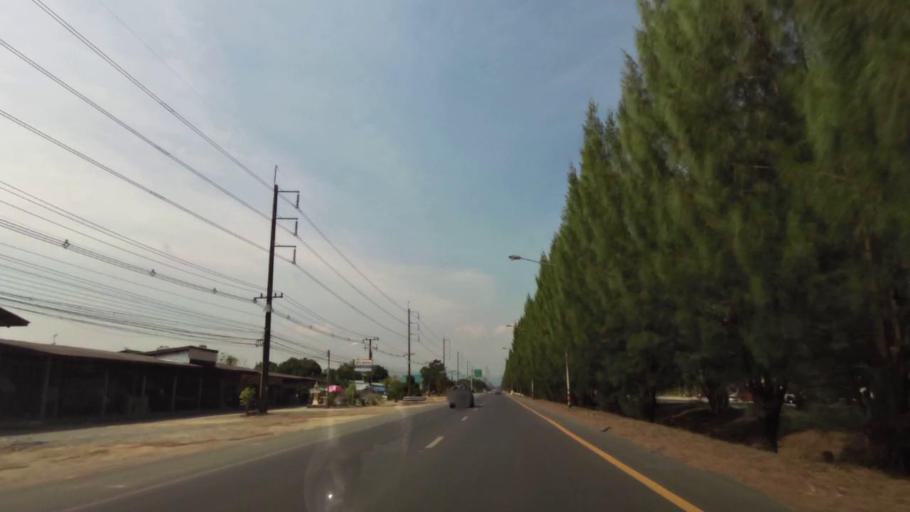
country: TH
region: Chanthaburi
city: Chanthaburi
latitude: 12.6308
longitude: 102.1442
